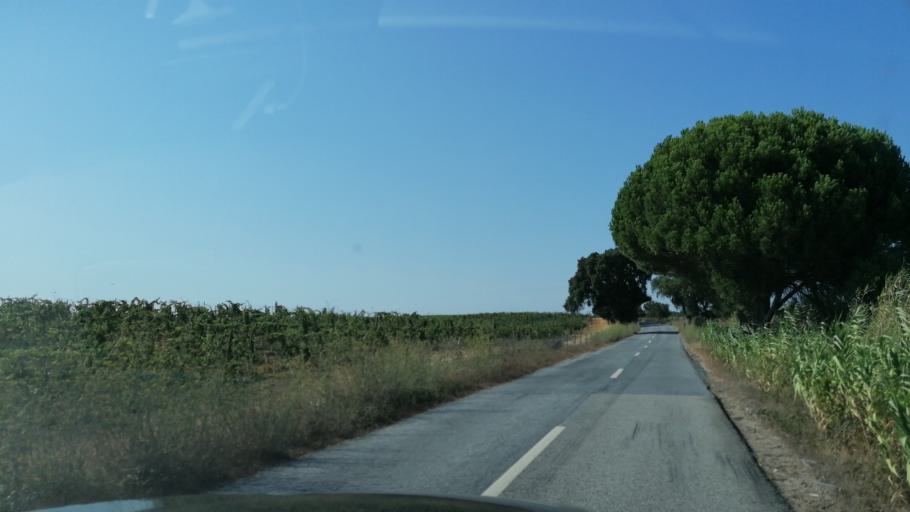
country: PT
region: Evora
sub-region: Vendas Novas
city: Vendas Novas
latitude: 38.7368
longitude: -8.6257
